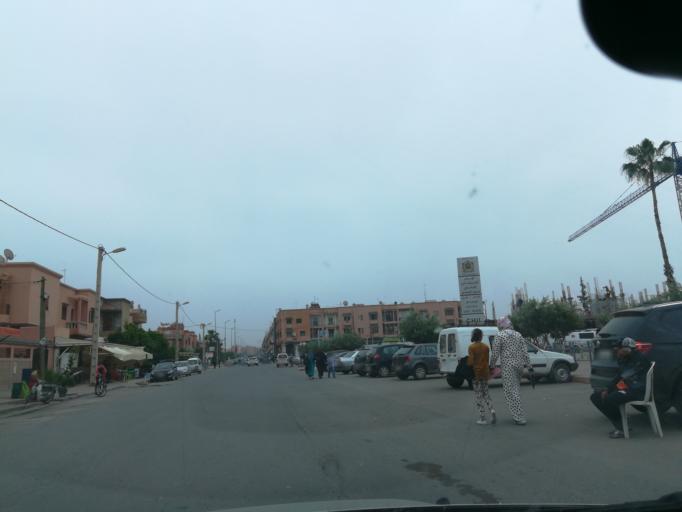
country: MA
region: Marrakech-Tensift-Al Haouz
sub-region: Marrakech
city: Marrakesh
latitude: 31.6638
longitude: -7.9941
